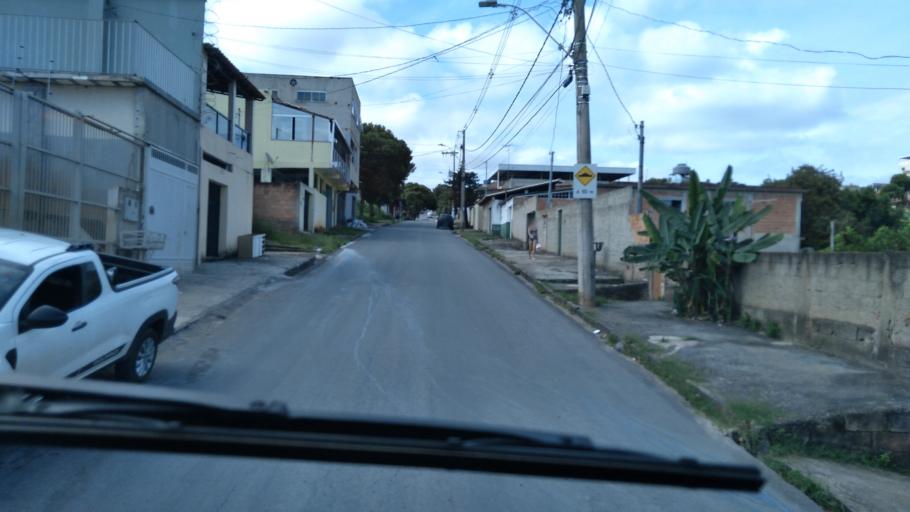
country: BR
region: Minas Gerais
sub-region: Santa Luzia
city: Santa Luzia
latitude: -19.8306
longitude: -43.8961
